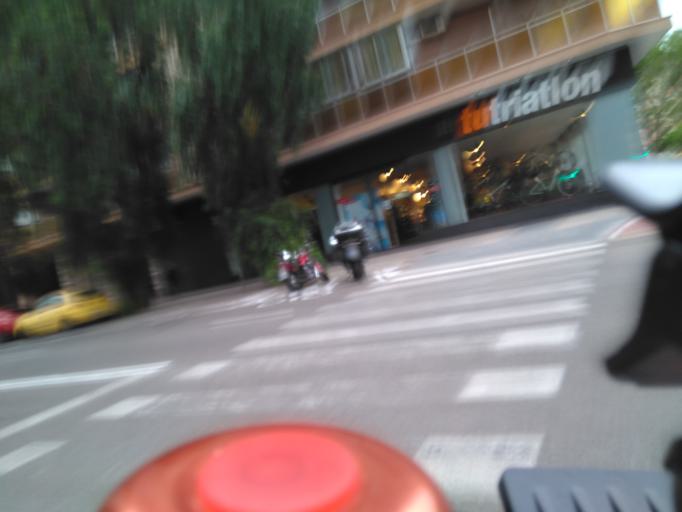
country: ES
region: Valencia
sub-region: Provincia de Valencia
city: Mislata
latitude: 39.4775
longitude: -0.3980
